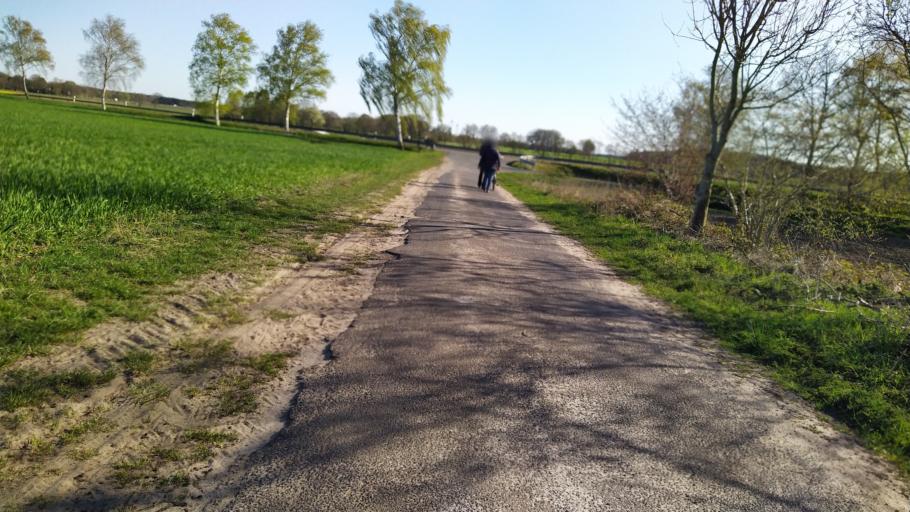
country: DE
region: Lower Saxony
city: Gross Meckelsen
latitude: 53.2894
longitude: 9.4648
